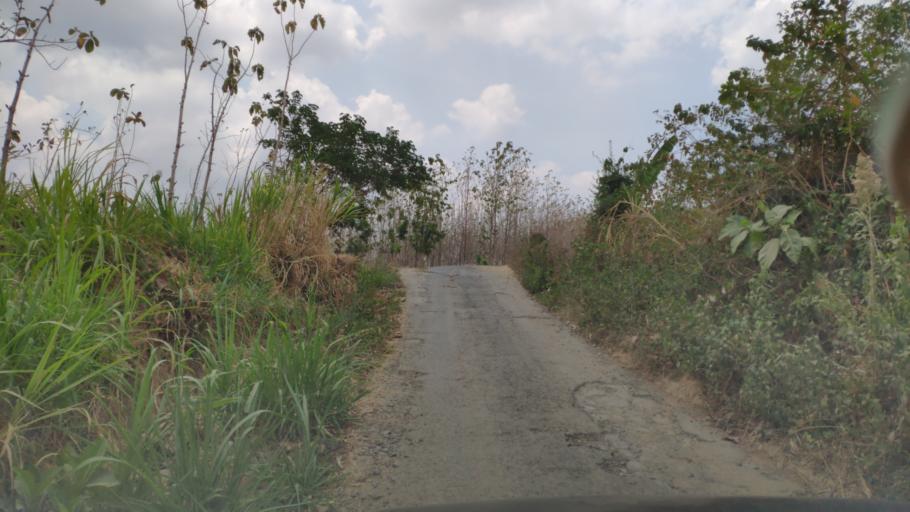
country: ID
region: Central Java
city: Kedungbacin
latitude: -6.8788
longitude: 111.2225
